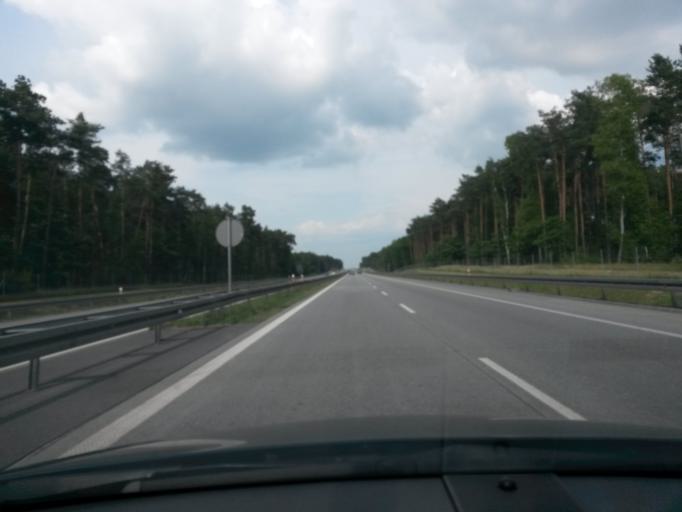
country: PL
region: Lodz Voivodeship
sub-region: Powiat tomaszowski
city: Lubochnia
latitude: 51.6302
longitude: 20.1042
